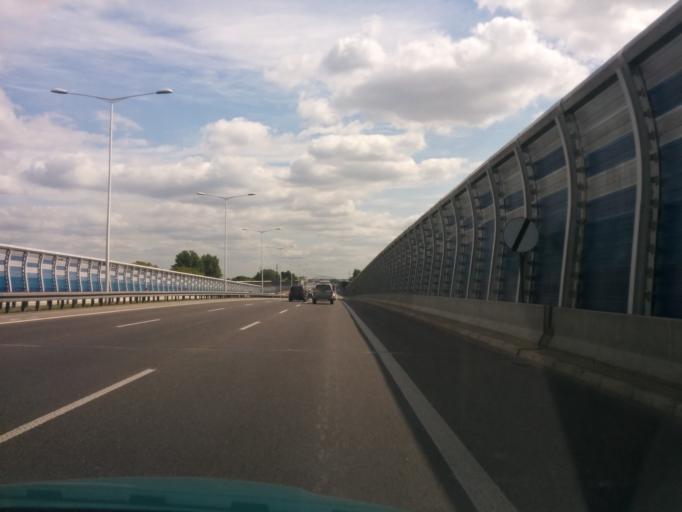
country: PL
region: Masovian Voivodeship
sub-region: Warszawa
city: Targowek
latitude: 52.2997
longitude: 21.0329
